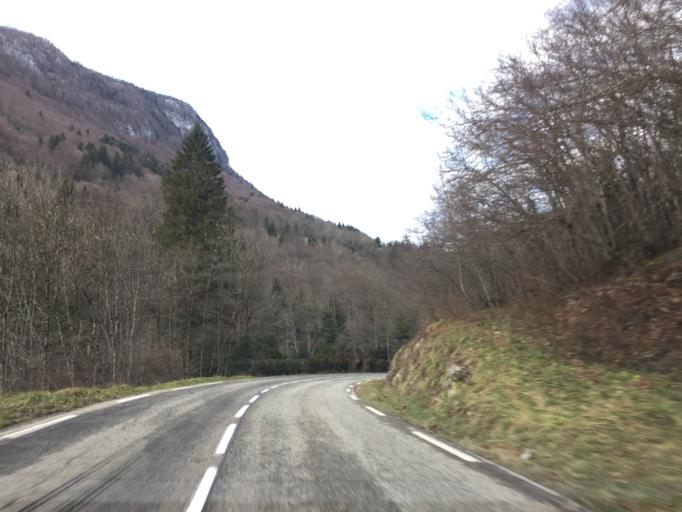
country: FR
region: Rhone-Alpes
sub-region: Departement de la Haute-Savoie
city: Gruffy
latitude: 45.7284
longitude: 6.0956
